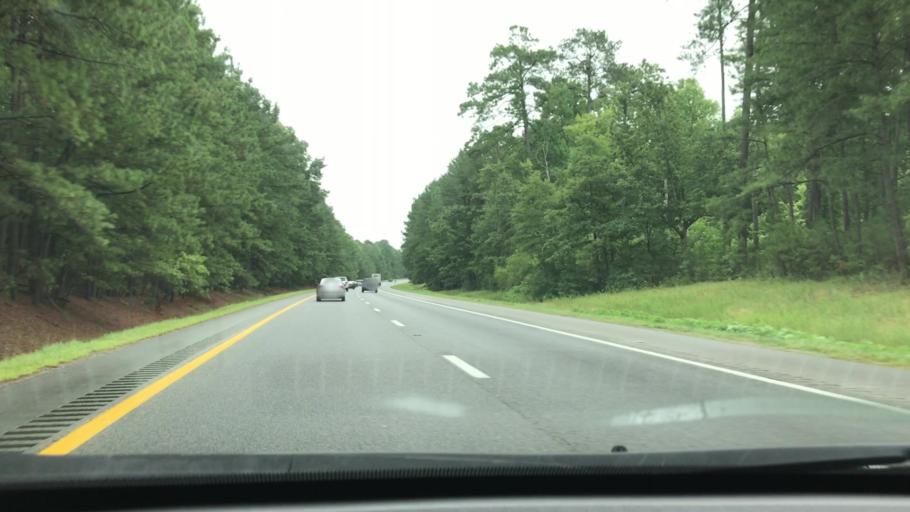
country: US
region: Virginia
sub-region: City of Emporia
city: Emporia
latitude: 36.7479
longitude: -77.5127
